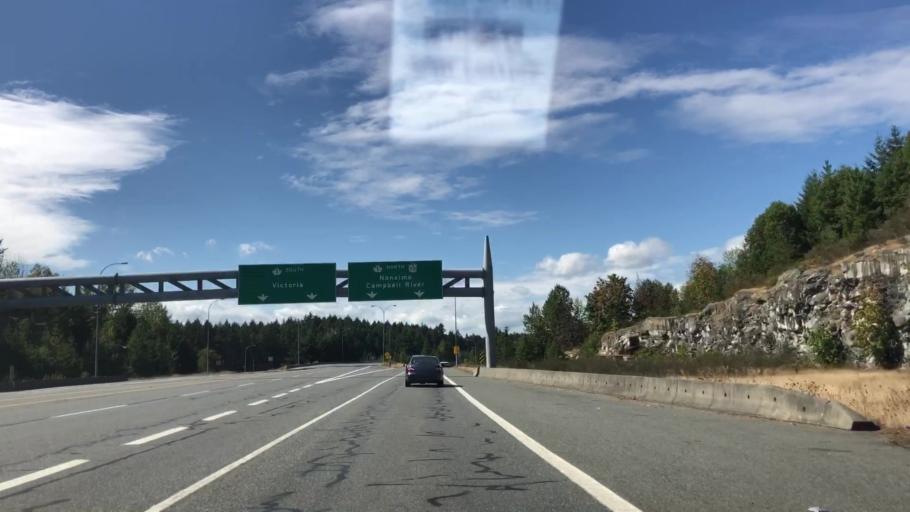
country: CA
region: British Columbia
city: Nanaimo
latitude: 49.1120
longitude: -123.8967
